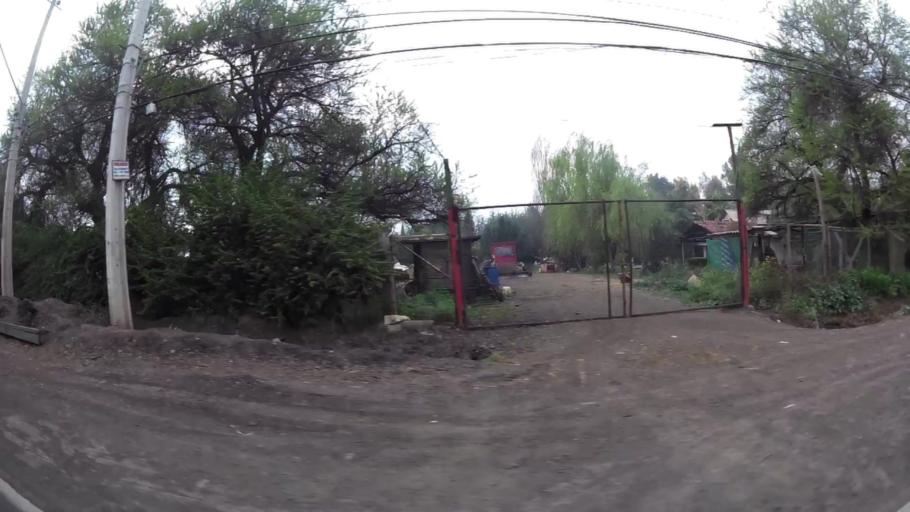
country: CL
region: Santiago Metropolitan
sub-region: Provincia de Chacabuco
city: Chicureo Abajo
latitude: -33.2549
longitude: -70.7629
